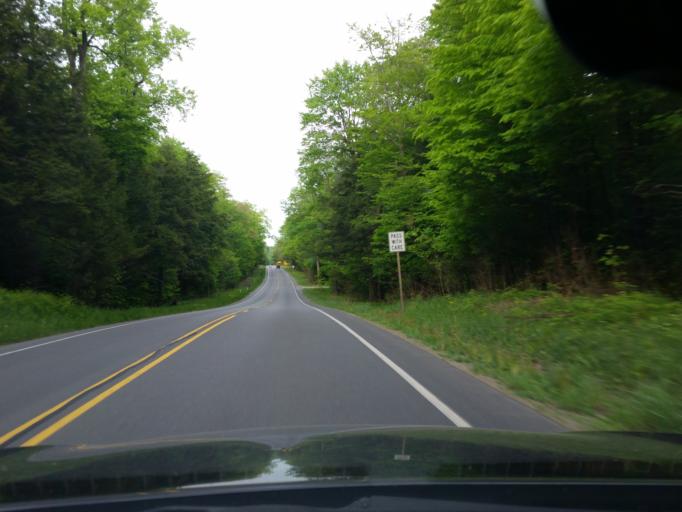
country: US
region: Pennsylvania
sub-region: McKean County
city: Kane
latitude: 41.5698
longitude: -78.8972
